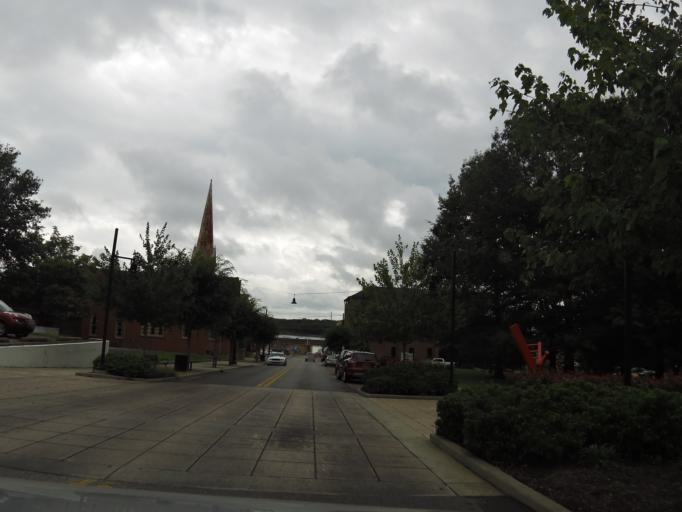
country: US
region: Missouri
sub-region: Cape Girardeau County
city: Cape Girardeau
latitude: 37.3061
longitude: -89.5202
